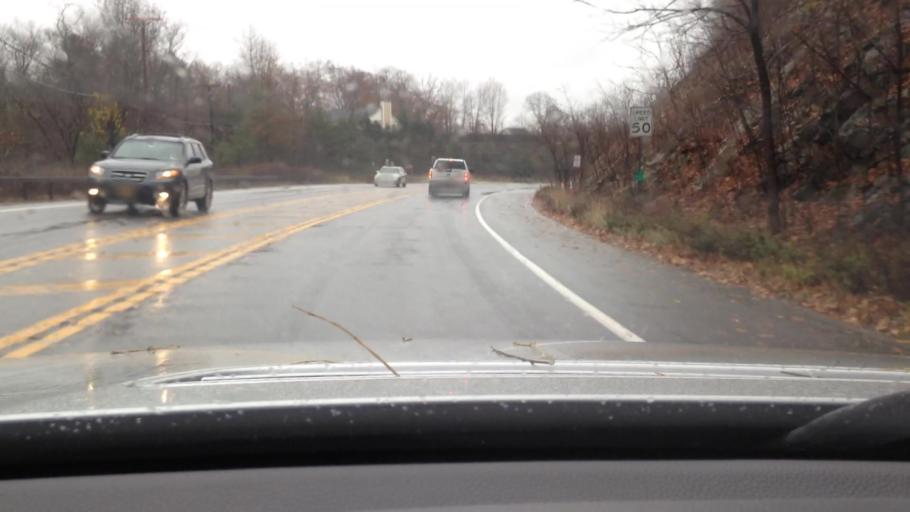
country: US
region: New York
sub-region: Westchester County
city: Peekskill
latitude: 41.3398
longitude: -73.9236
